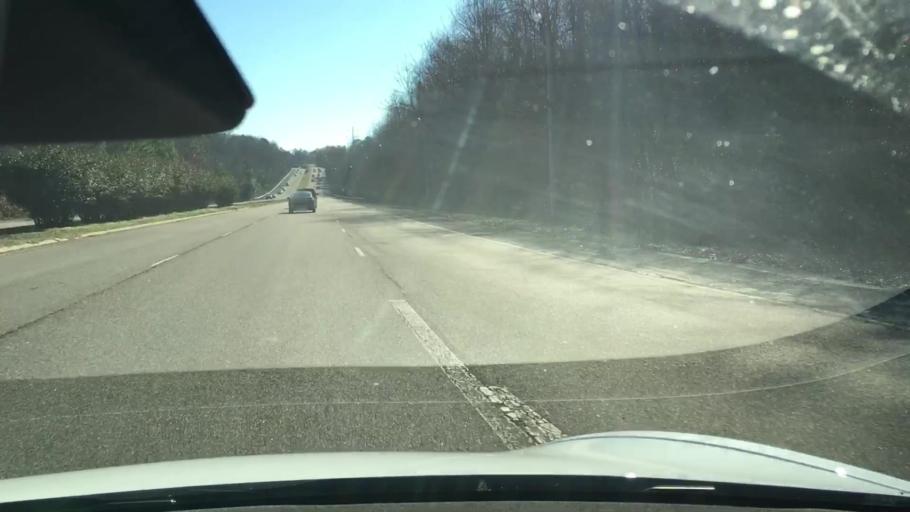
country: US
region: Virginia
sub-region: Chesterfield County
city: Bon Air
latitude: 37.5493
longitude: -77.5654
